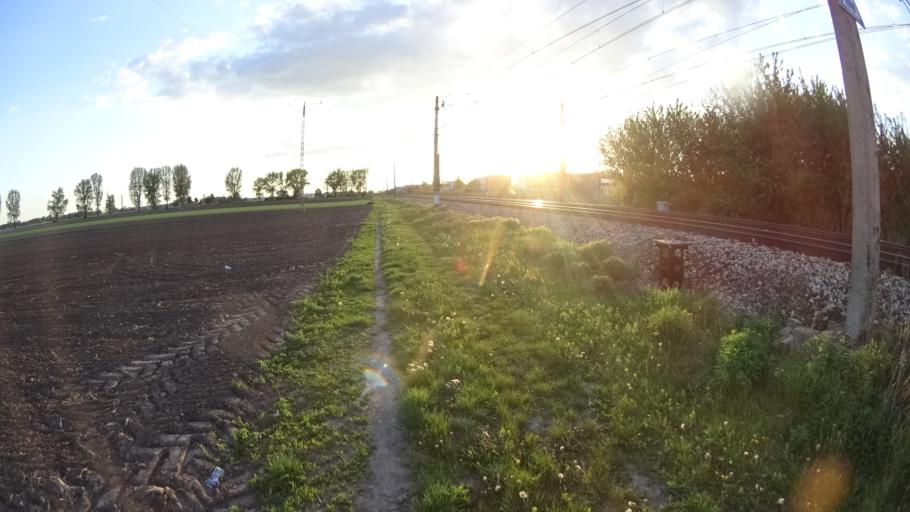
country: PL
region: Masovian Voivodeship
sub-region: Powiat pruszkowski
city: Piastow
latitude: 52.2065
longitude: 20.8241
